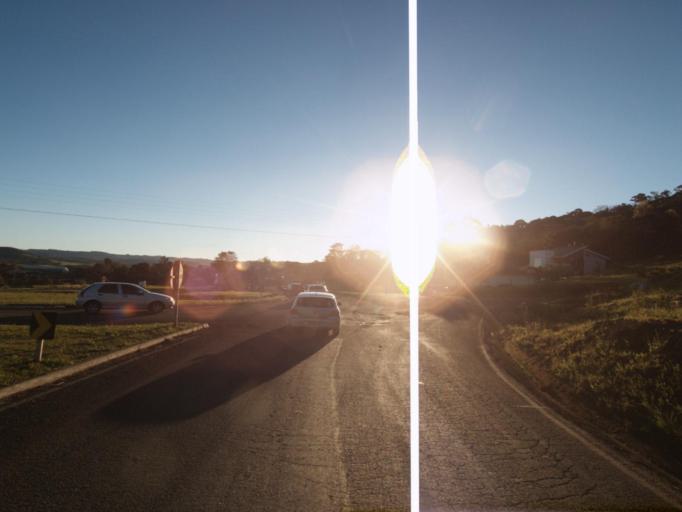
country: BR
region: Santa Catarina
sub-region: Sao Lourenco Do Oeste
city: Sao Lourenco dOeste
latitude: -26.8258
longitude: -53.0915
